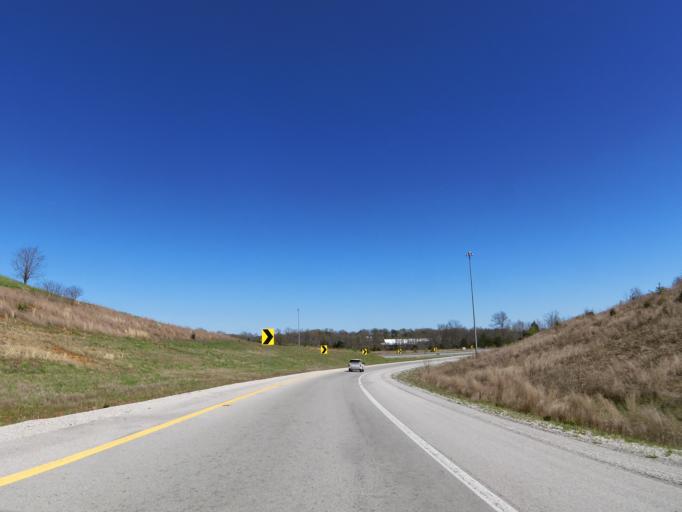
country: US
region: Kentucky
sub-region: Pulaski County
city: Somerset
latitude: 37.1240
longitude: -84.6386
